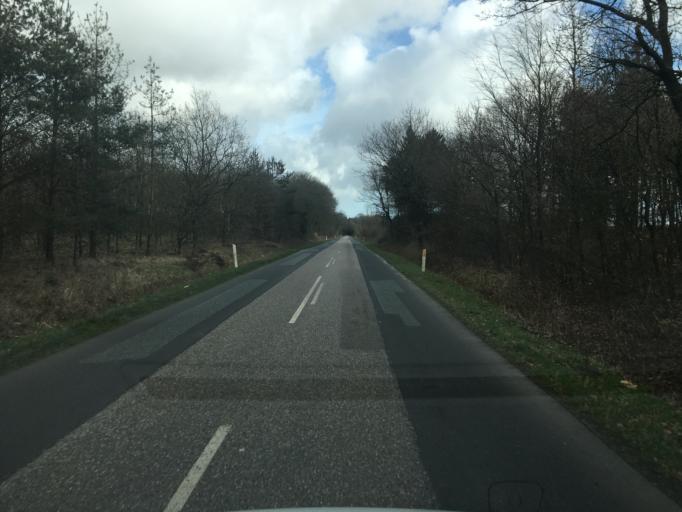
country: DK
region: South Denmark
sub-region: Aabenraa Kommune
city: Krusa
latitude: 54.8991
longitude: 9.4612
